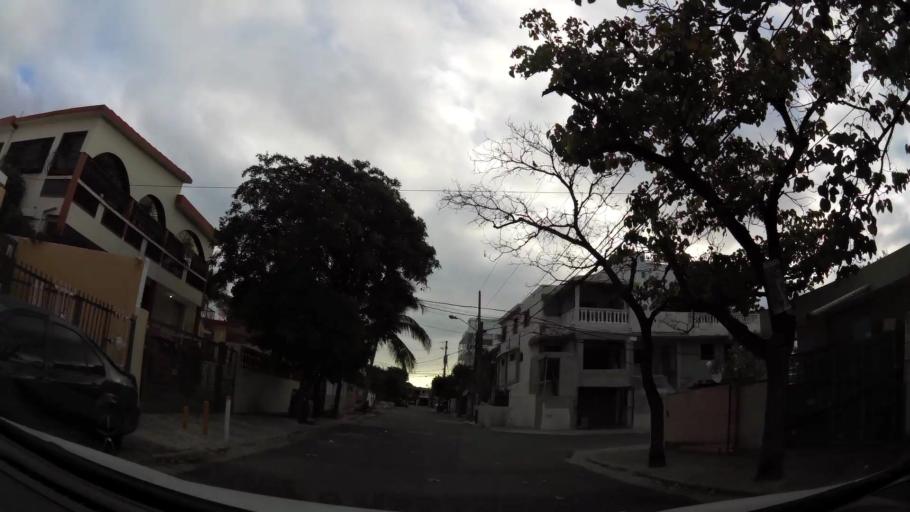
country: DO
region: Nacional
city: Bella Vista
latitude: 18.4314
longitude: -69.9594
